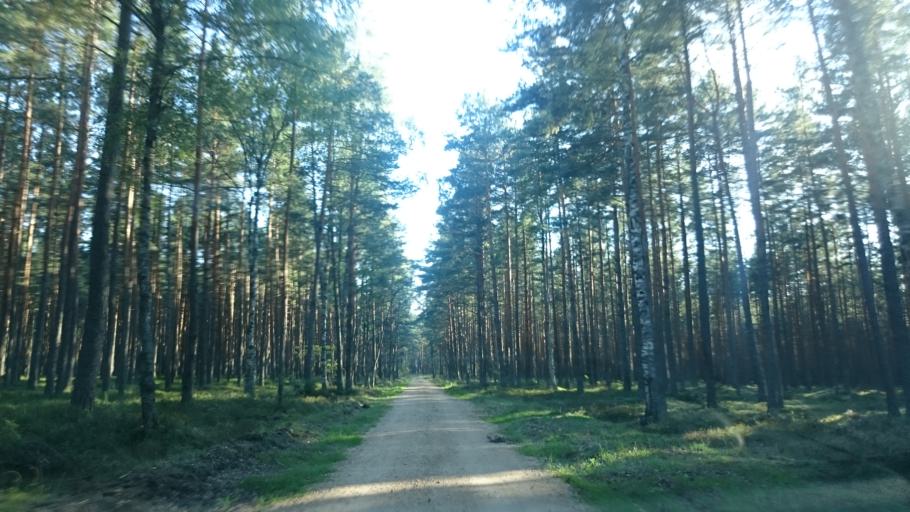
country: LV
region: Carnikava
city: Carnikava
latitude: 57.1114
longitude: 24.2408
